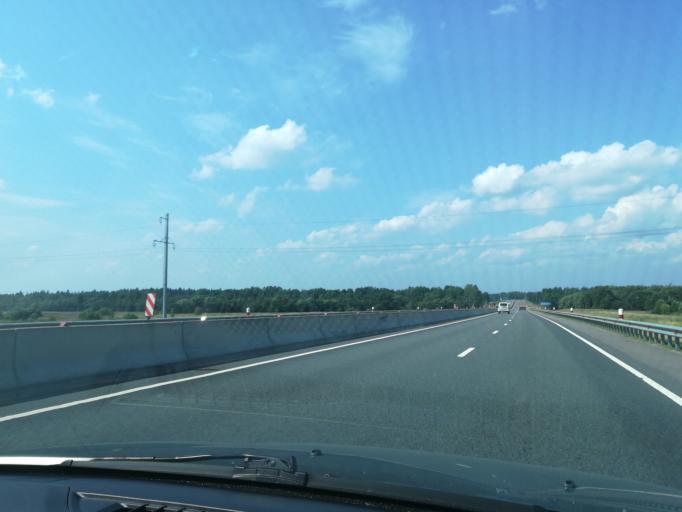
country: RU
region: Leningrad
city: Kingisepp
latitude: 59.5952
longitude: 28.7366
